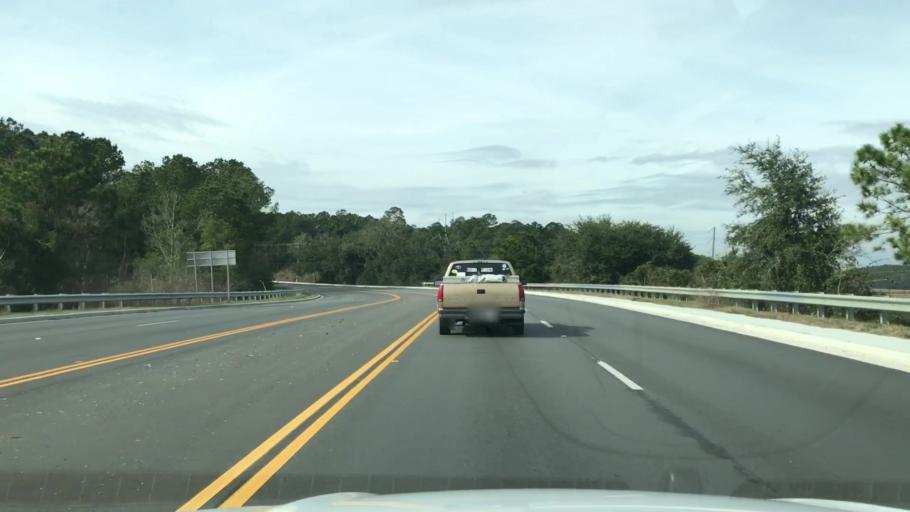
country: US
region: South Carolina
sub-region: Charleston County
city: Shell Point
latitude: 32.7517
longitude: -80.0278
